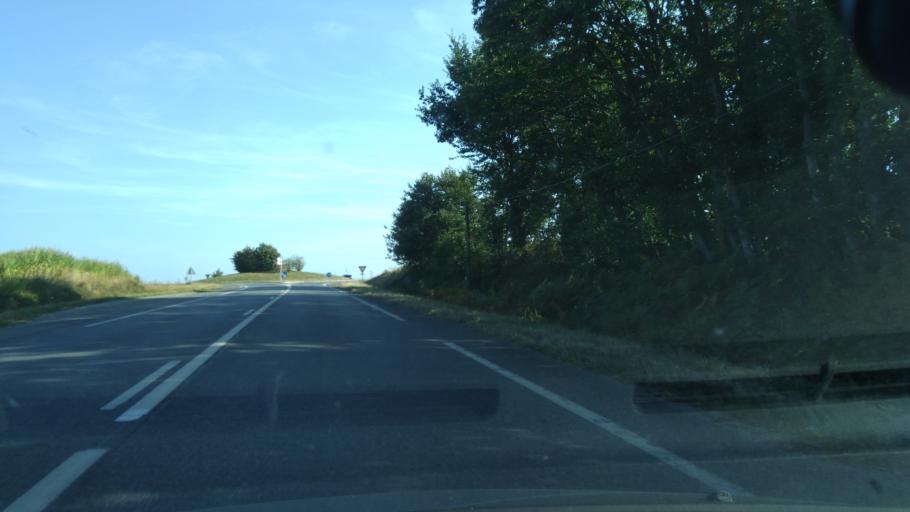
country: FR
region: Pays de la Loire
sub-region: Departement de la Mayenne
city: Entrammes
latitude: 48.0161
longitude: -0.7305
